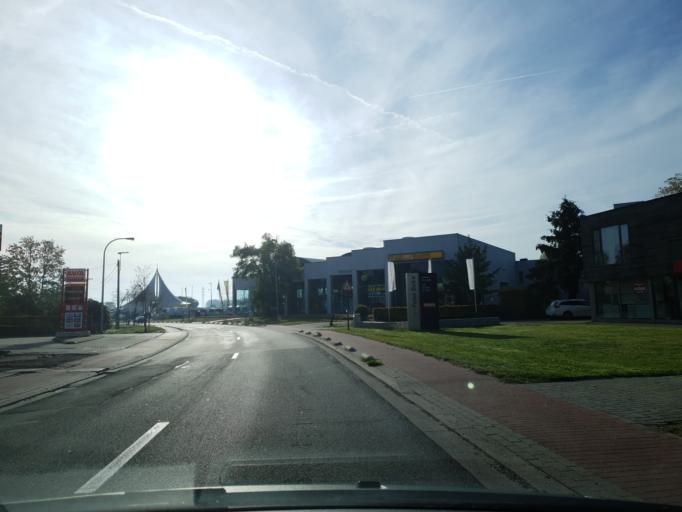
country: BE
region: Flanders
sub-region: Provincie Oost-Vlaanderen
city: Temse
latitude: 51.1371
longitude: 4.1859
